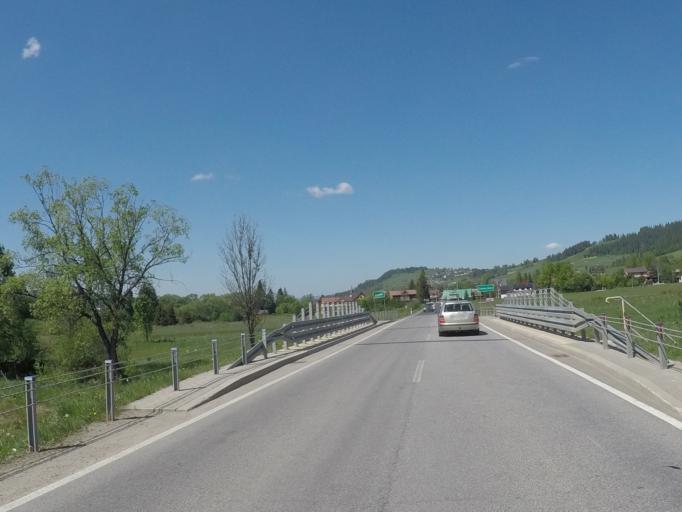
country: PL
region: Lesser Poland Voivodeship
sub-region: Powiat tatrzanski
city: Czarna Gora
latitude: 49.3525
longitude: 20.1349
